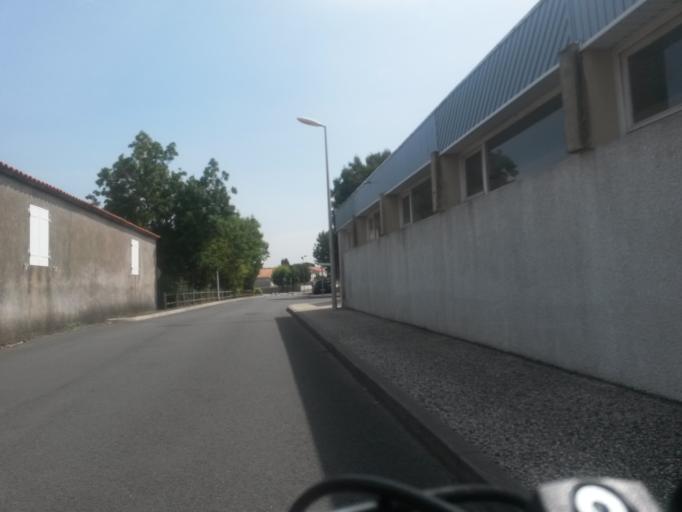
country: FR
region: Poitou-Charentes
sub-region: Departement de la Charente-Maritime
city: Nieul-sur-Mer
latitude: 46.1947
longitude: -1.1859
